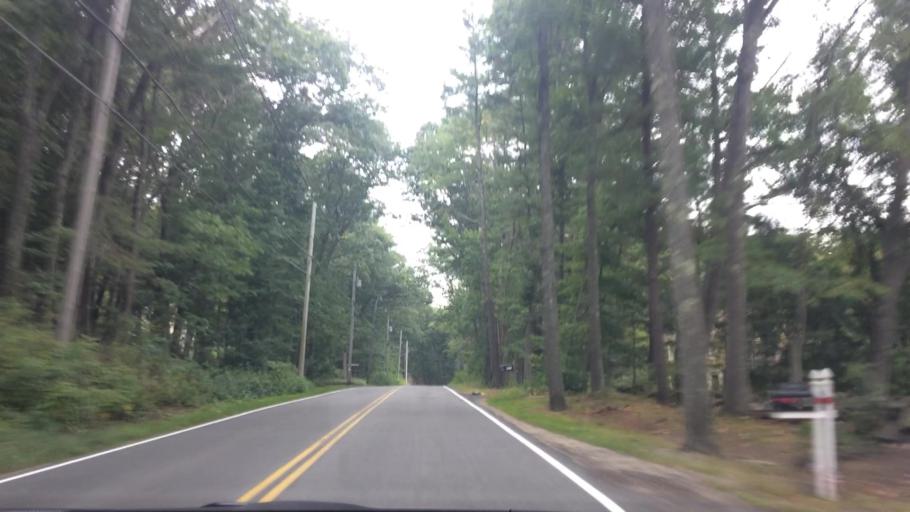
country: US
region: Massachusetts
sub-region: Essex County
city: Boxford
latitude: 42.6962
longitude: -71.0355
